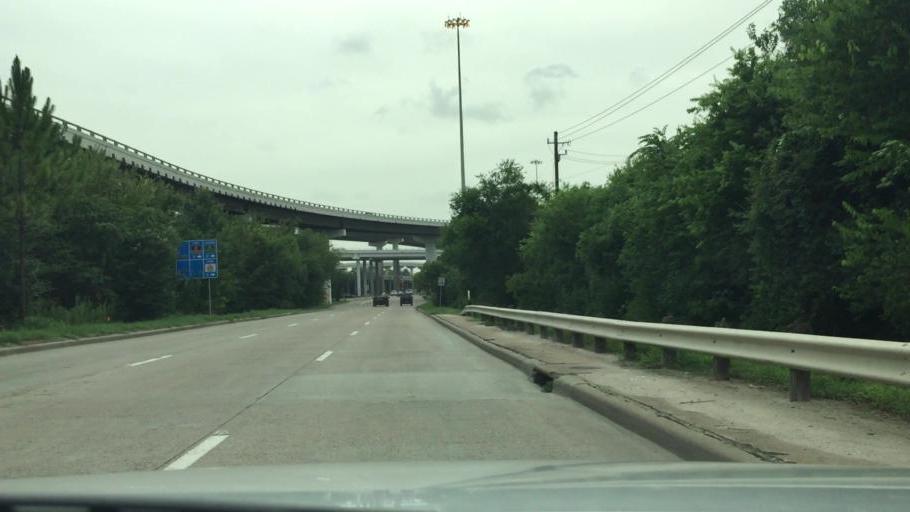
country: US
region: Texas
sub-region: Harris County
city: Cloverleaf
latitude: 29.7724
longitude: -95.1504
